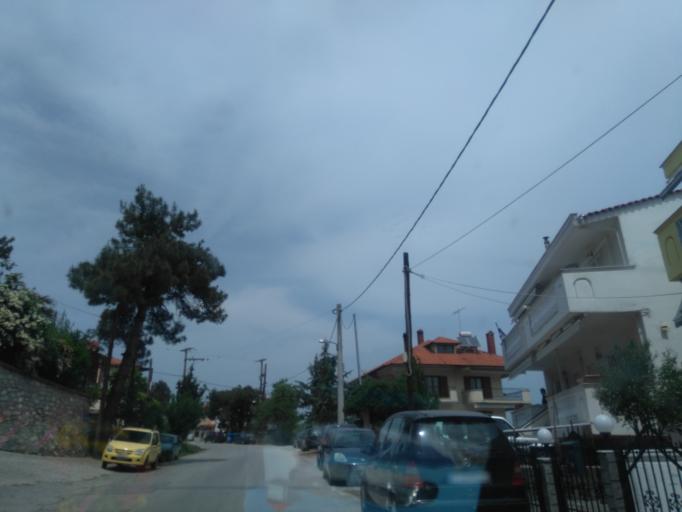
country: GR
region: Central Macedonia
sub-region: Nomos Thessalonikis
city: Lagyna
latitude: 40.7243
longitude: 22.9969
